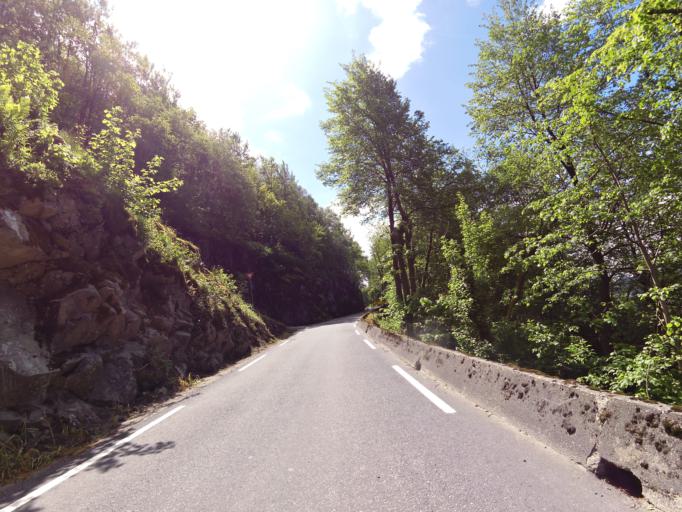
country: NO
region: Vest-Agder
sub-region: Kvinesdal
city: Liknes
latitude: 58.2920
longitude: 6.9412
